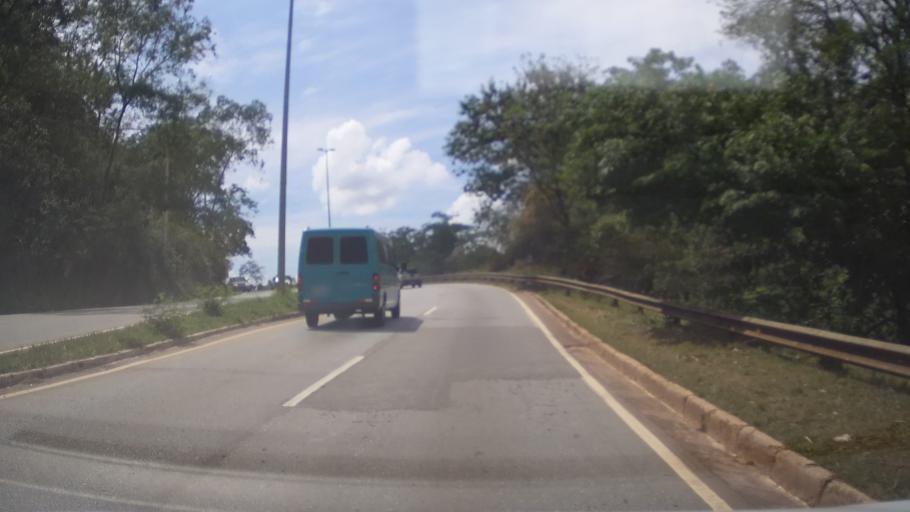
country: BR
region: Minas Gerais
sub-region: Nova Lima
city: Nova Lima
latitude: -19.9963
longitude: -43.9173
